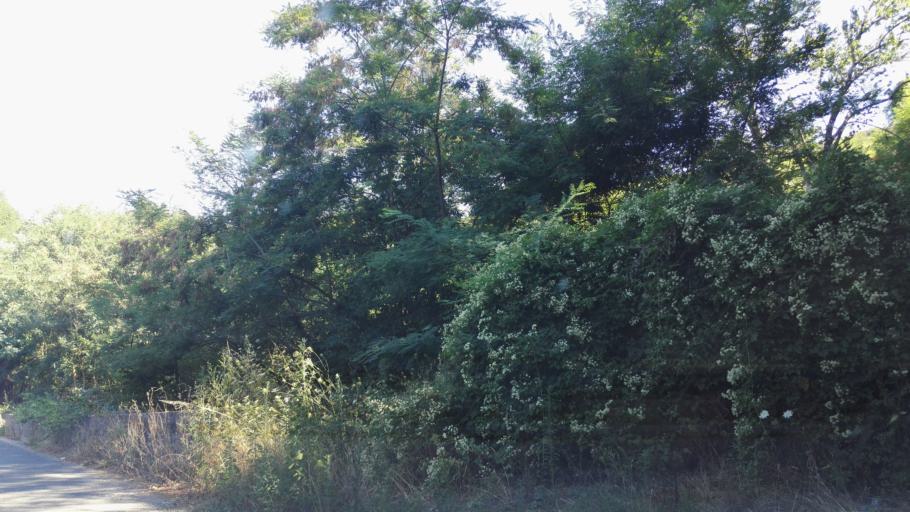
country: IT
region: Calabria
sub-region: Provincia di Vibo-Valentia
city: Sorianello
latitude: 38.5911
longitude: 16.2511
